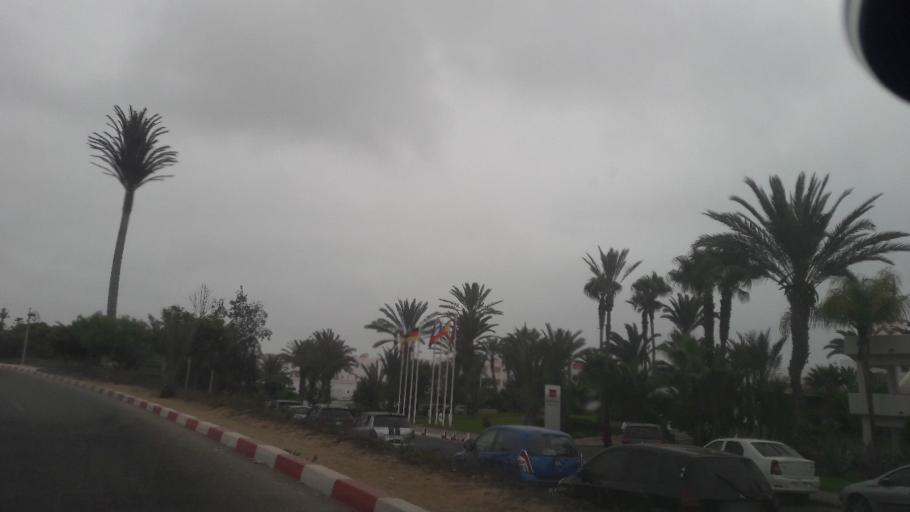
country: MA
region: Souss-Massa-Draa
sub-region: Agadir-Ida-ou-Tnan
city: Agadir
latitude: 30.3991
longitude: -9.5973
